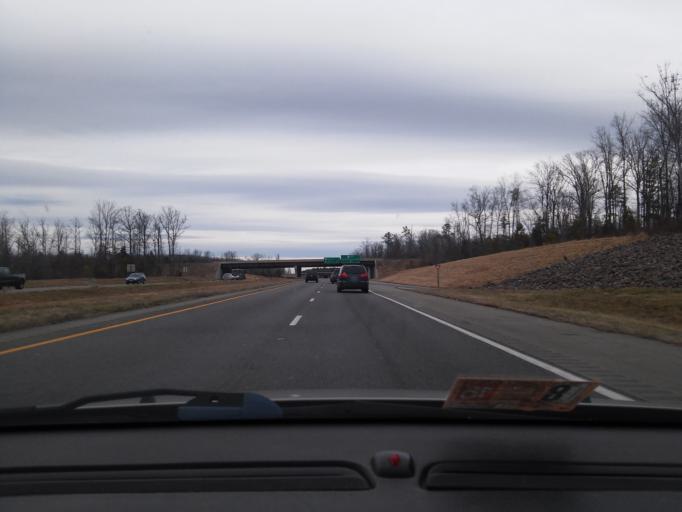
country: US
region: Virginia
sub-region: Henrico County
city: Short Pump
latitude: 37.6298
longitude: -77.6635
